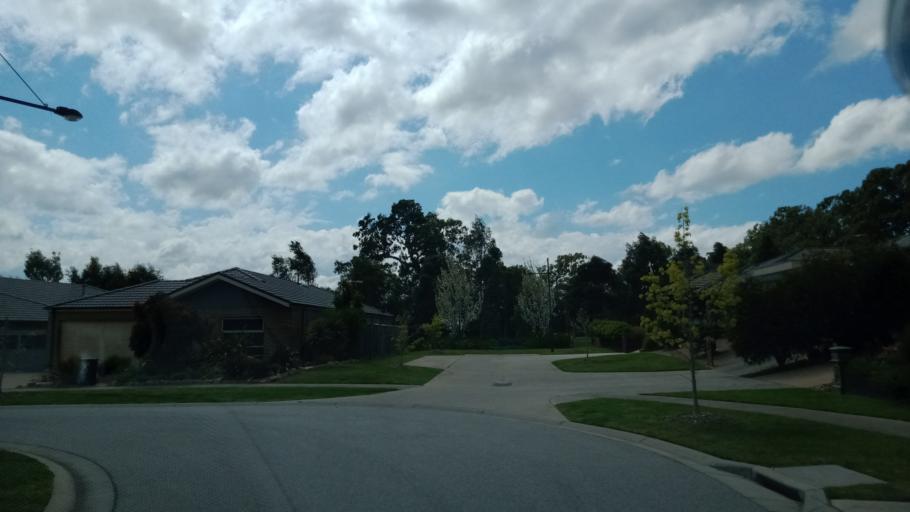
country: AU
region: Victoria
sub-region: Frankston
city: Sandhurst
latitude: -38.0873
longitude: 145.1995
